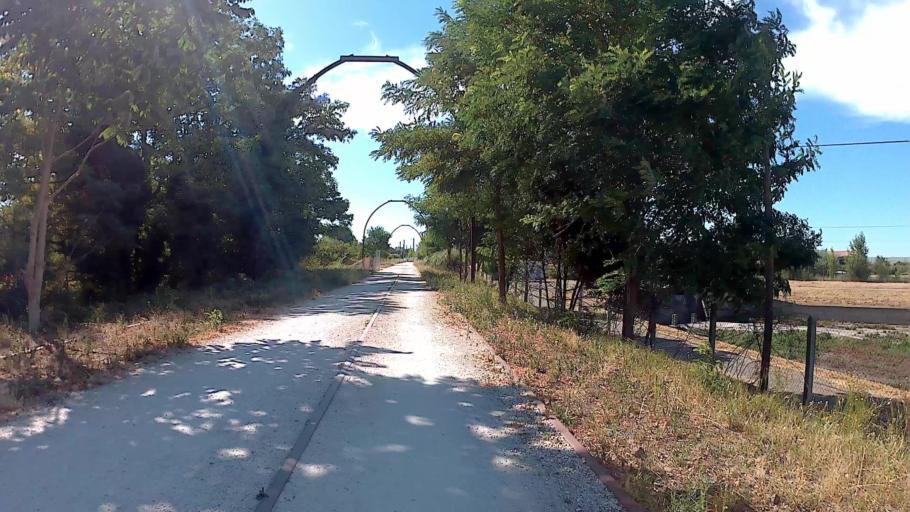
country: FR
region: Aquitaine
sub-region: Departement de la Gironde
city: Le Bouscat
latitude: 44.8704
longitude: -0.5865
